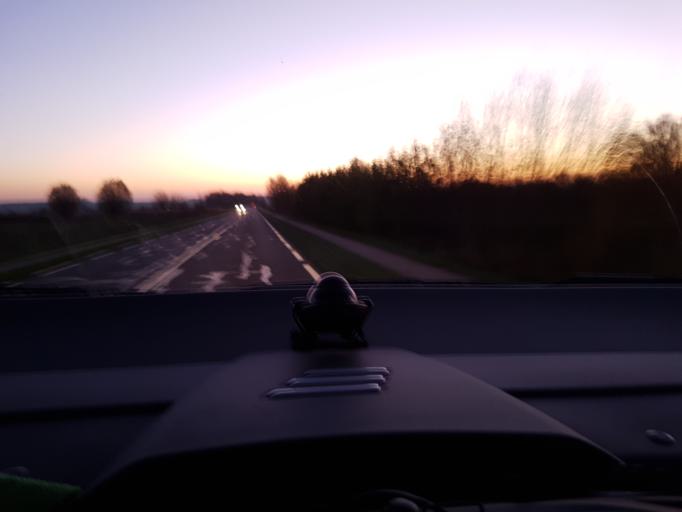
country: FR
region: Picardie
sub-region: Departement de la Somme
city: Saint-Valery-sur-Somme
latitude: 50.1792
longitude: 1.6913
